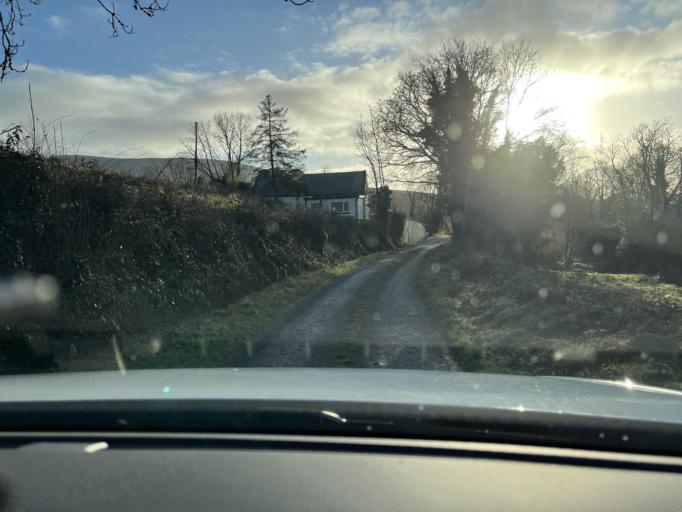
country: IE
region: Connaught
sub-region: County Leitrim
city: Manorhamilton
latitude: 54.2110
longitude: -7.9678
